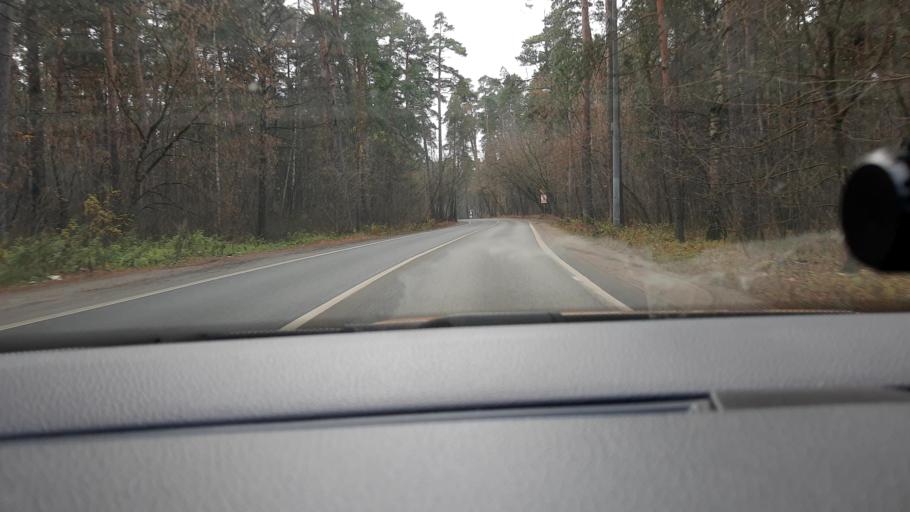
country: RU
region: Moscow
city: Rublevo
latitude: 55.7784
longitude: 37.3572
